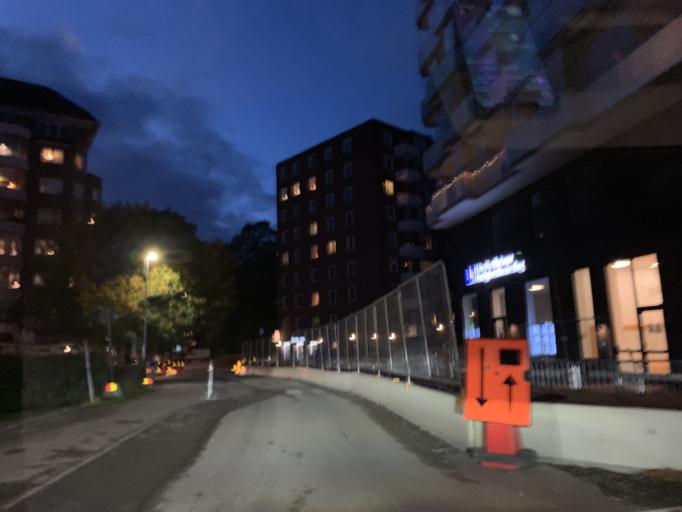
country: SE
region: Stockholm
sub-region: Huddinge Kommun
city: Huddinge
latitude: 59.2339
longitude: 17.9868
